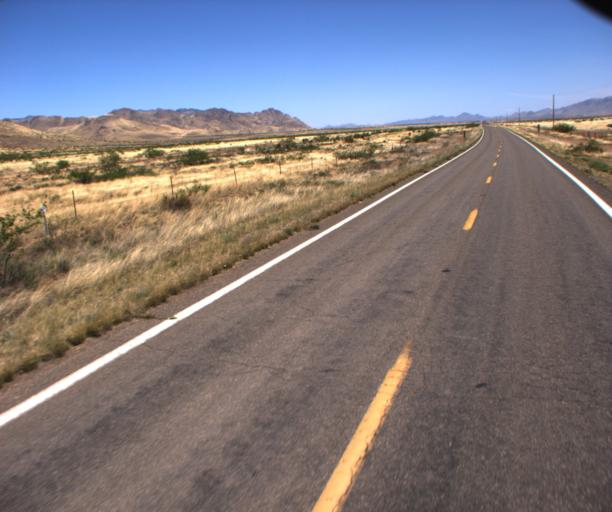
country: US
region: Arizona
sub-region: Cochise County
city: Douglas
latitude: 31.6557
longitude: -109.1571
